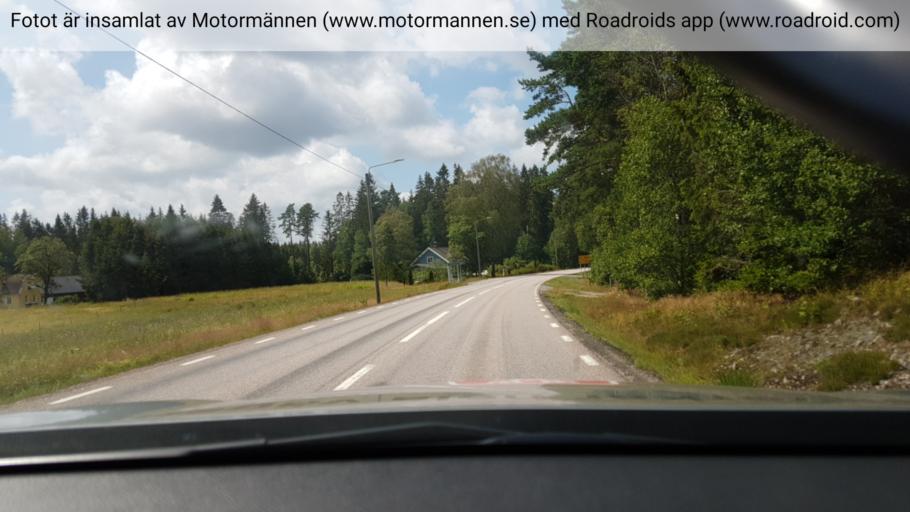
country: SE
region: Vaestra Goetaland
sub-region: Svenljunga Kommun
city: Svenljunga
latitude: 57.4889
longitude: 12.9599
